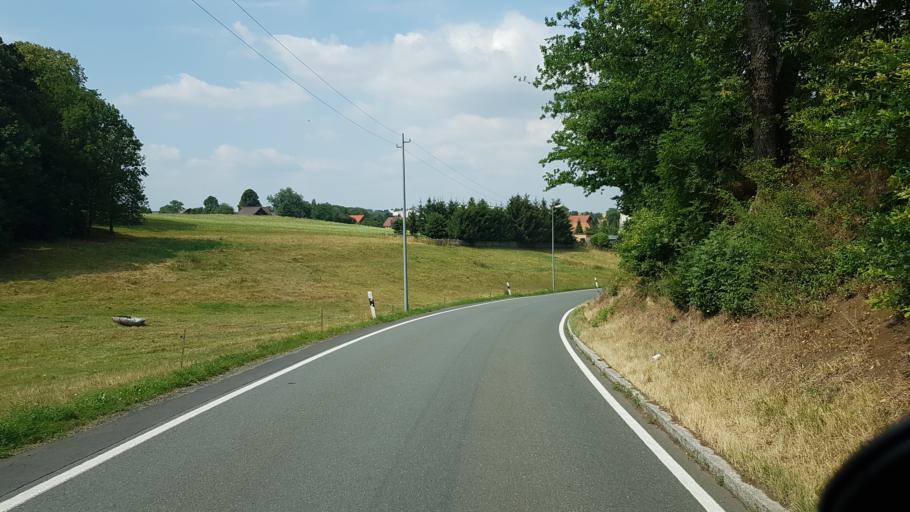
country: DE
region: Saxony
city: Lichtentanne
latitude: 50.6816
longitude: 12.4405
